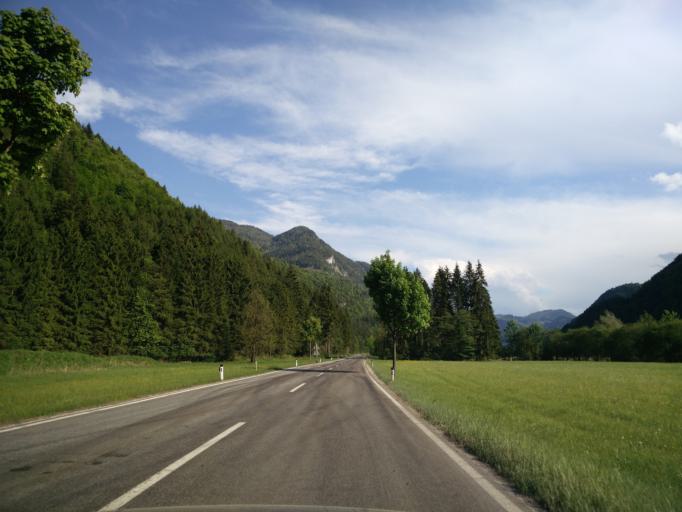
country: DE
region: Bavaria
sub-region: Upper Bavaria
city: Reit im Winkl
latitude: 47.6341
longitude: 12.4614
